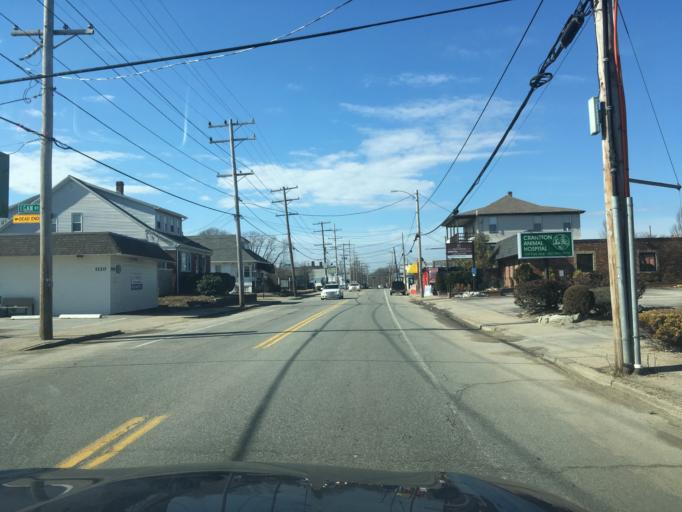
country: US
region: Rhode Island
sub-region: Providence County
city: Cranston
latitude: 41.7829
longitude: -71.4473
